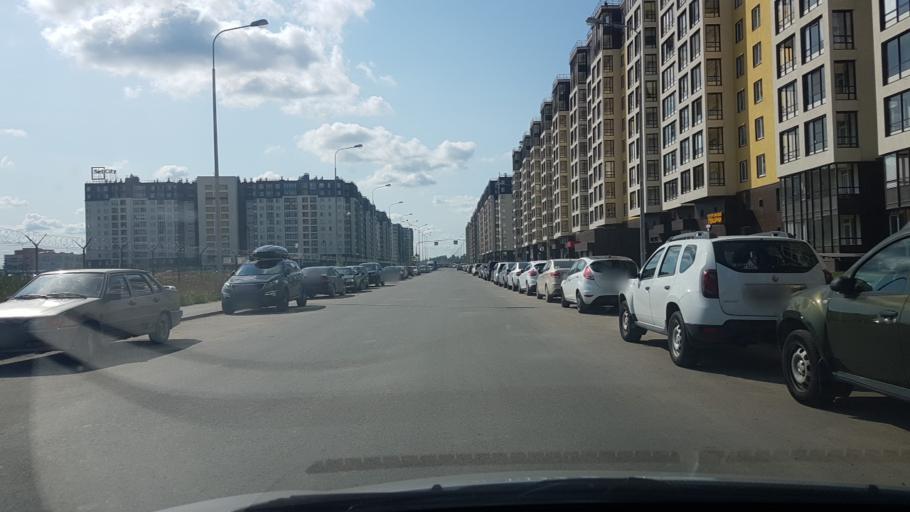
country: RU
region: St.-Petersburg
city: Sosnovaya Polyana
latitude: 59.8423
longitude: 30.1137
